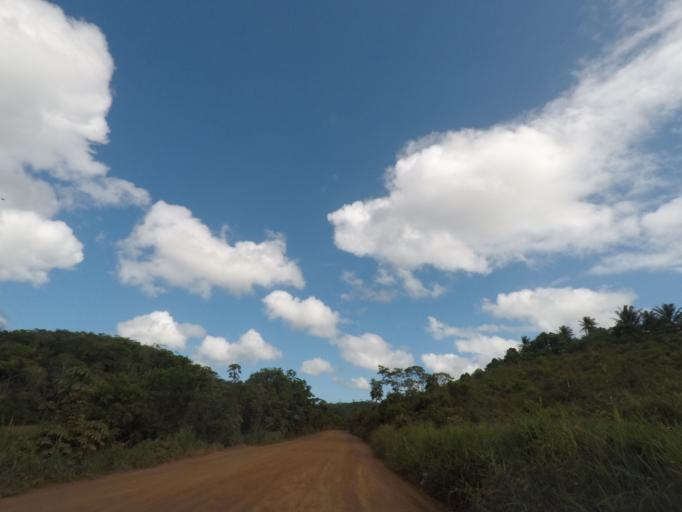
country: BR
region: Bahia
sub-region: Itacare
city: Itacare
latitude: -14.2191
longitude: -39.0838
